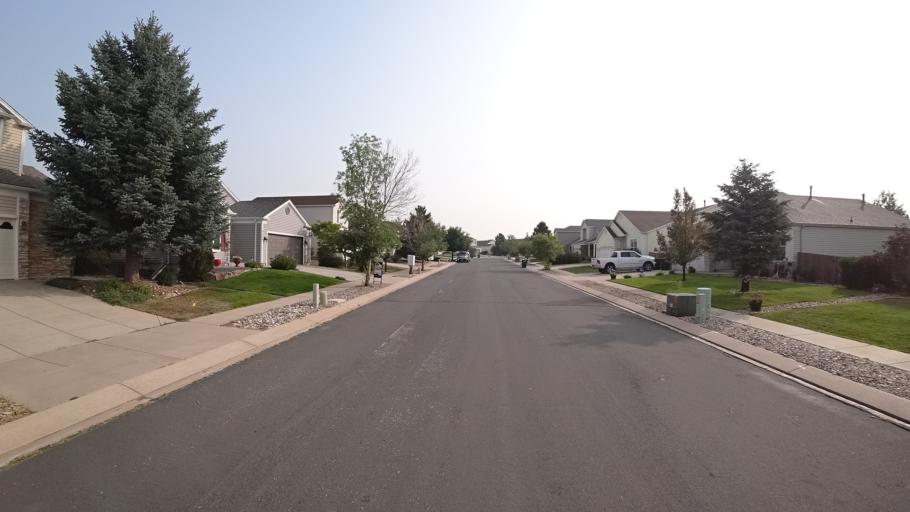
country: US
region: Colorado
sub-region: El Paso County
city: Cimarron Hills
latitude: 38.9313
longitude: -104.7283
